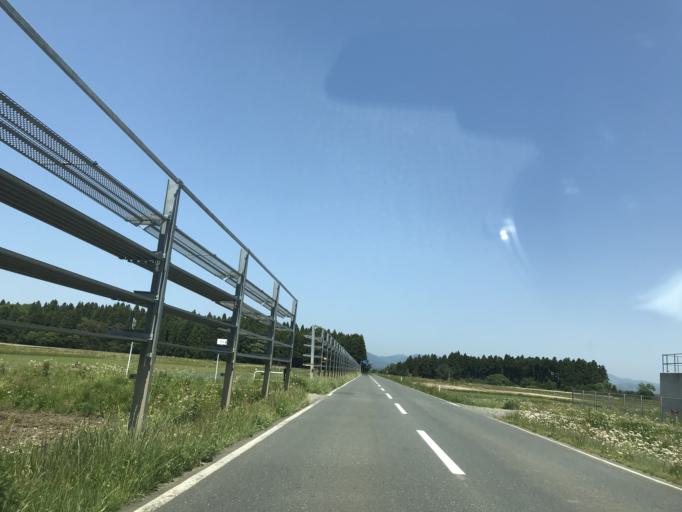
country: JP
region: Iwate
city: Kitakami
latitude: 39.2732
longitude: 141.0532
